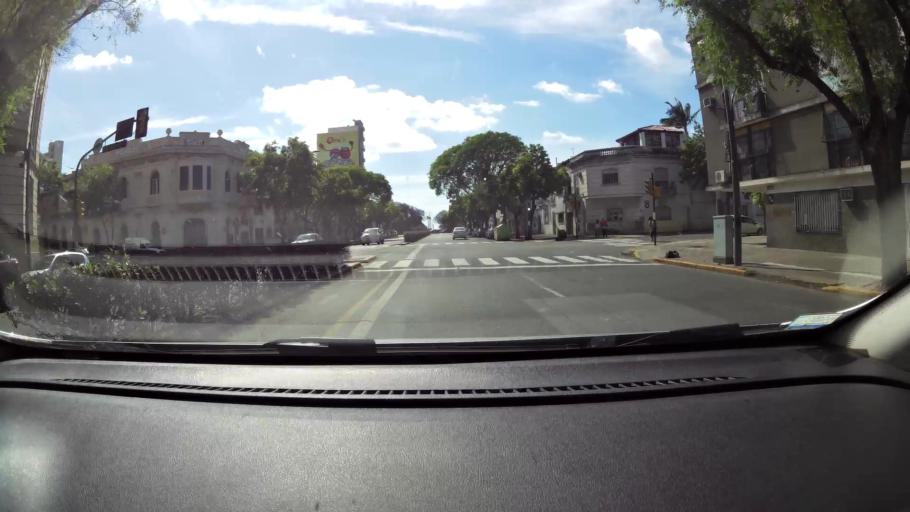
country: AR
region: Santa Fe
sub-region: Departamento de Rosario
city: Rosario
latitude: -32.9596
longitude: -60.6284
